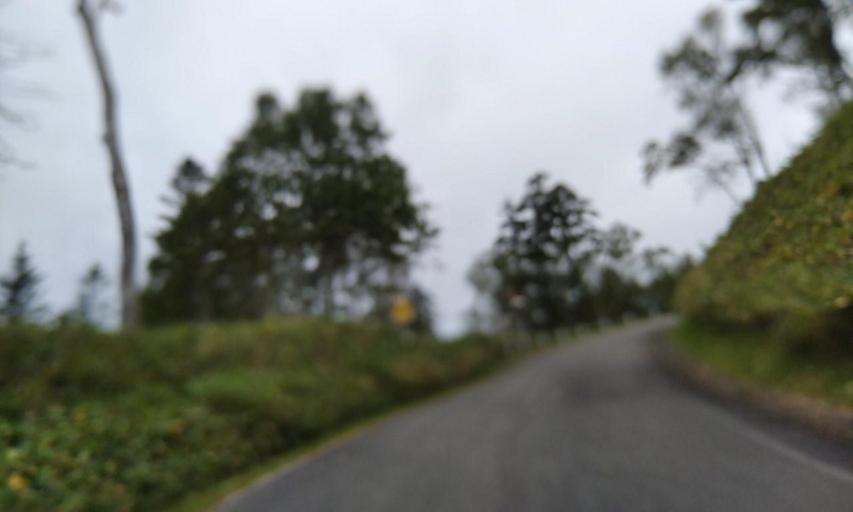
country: JP
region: Hokkaido
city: Bihoro
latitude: 43.5770
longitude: 144.2232
